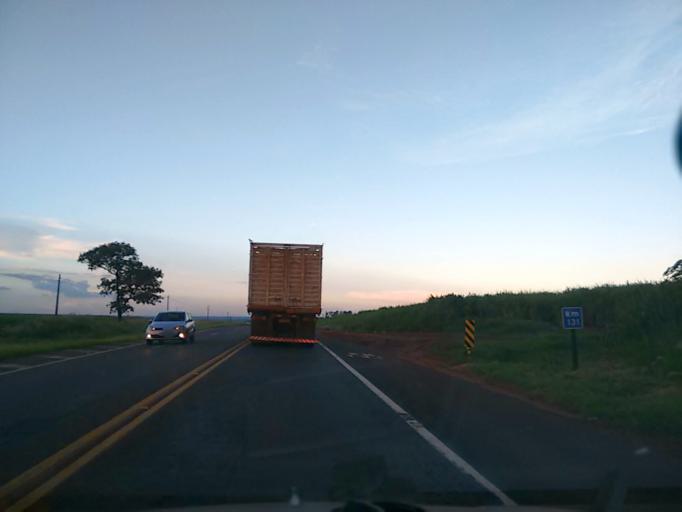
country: BR
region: Sao Paulo
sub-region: Boa Esperanca Do Sul
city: Boa Esperanca do Sul
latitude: -22.1354
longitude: -48.4610
